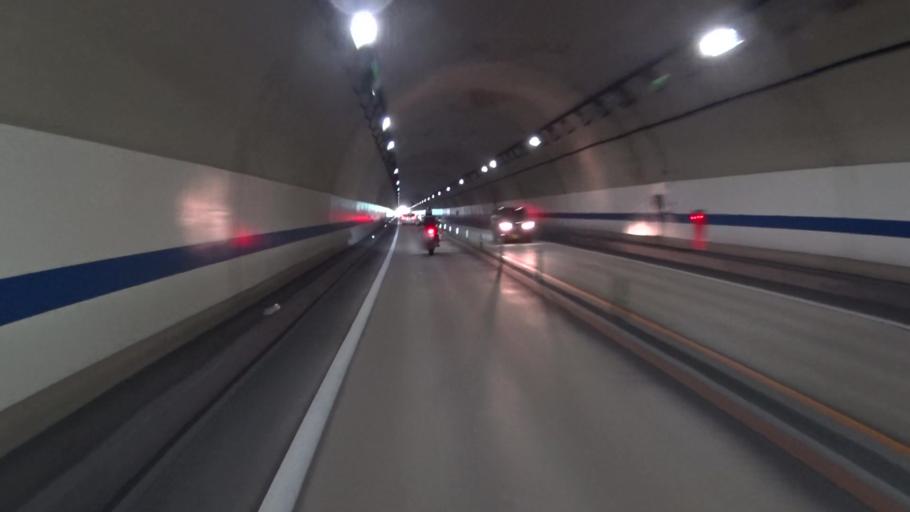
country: JP
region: Kyoto
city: Ayabe
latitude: 35.4122
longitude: 135.2239
